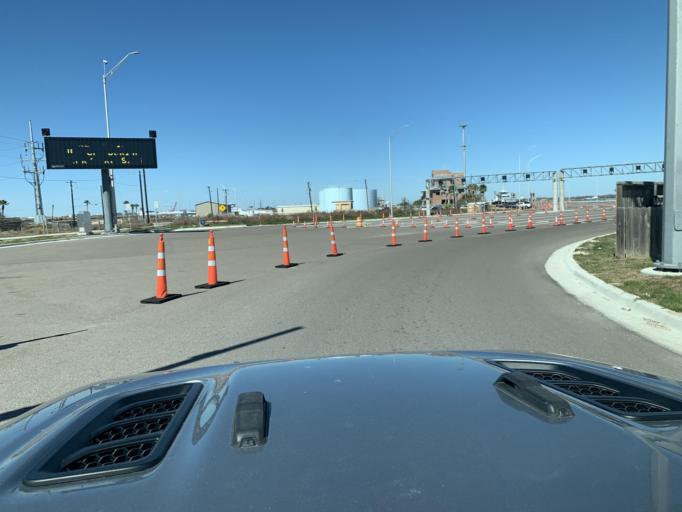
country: US
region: Texas
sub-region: Nueces County
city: Port Aransas
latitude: 27.8369
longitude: -97.0695
